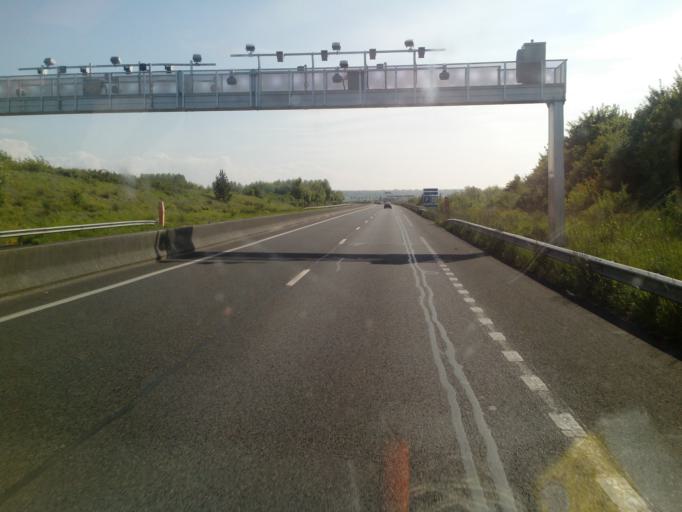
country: FR
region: Picardie
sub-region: Departement de la Somme
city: Bouttencourt
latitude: 49.9687
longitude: 1.6638
